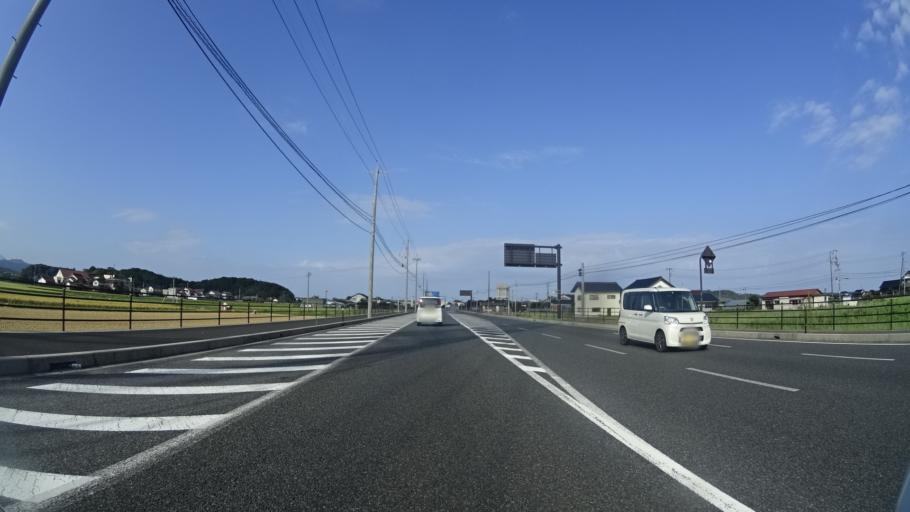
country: JP
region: Shimane
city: Izumo
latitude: 35.3376
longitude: 132.7009
